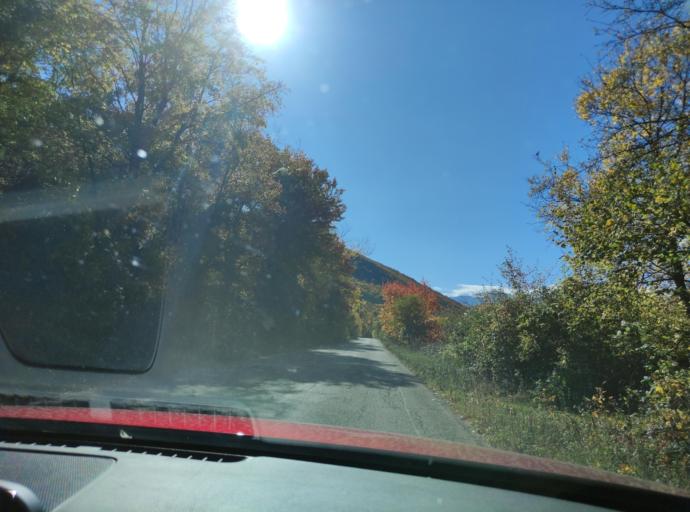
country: BG
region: Montana
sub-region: Obshtina Chiprovtsi
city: Chiprovtsi
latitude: 43.4201
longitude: 22.9536
